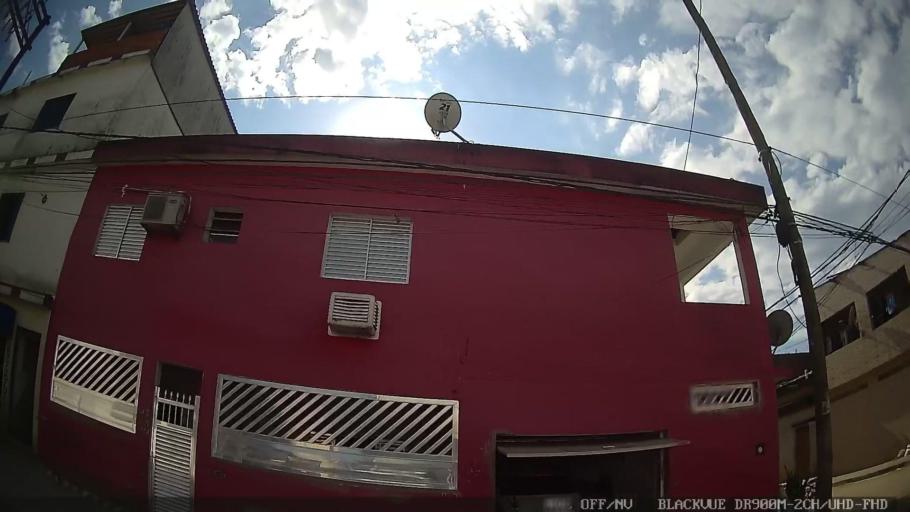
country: BR
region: Sao Paulo
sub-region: Guaruja
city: Guaruja
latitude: -23.9618
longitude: -46.2487
